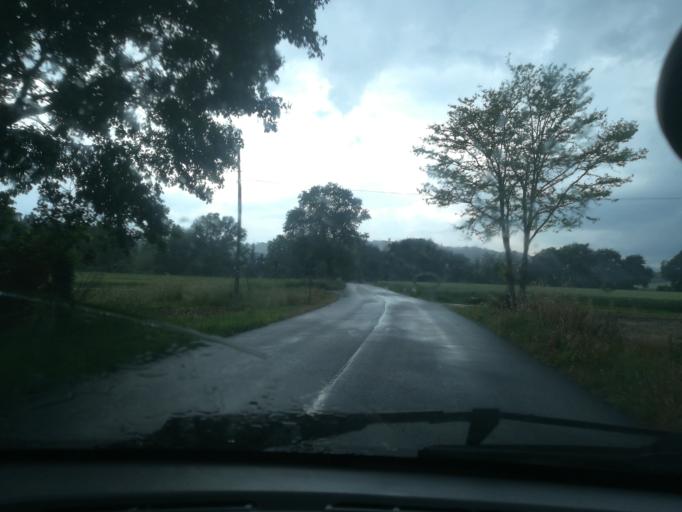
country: IT
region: The Marches
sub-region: Provincia di Macerata
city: Passo di Treia
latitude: 43.3106
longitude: 13.3444
